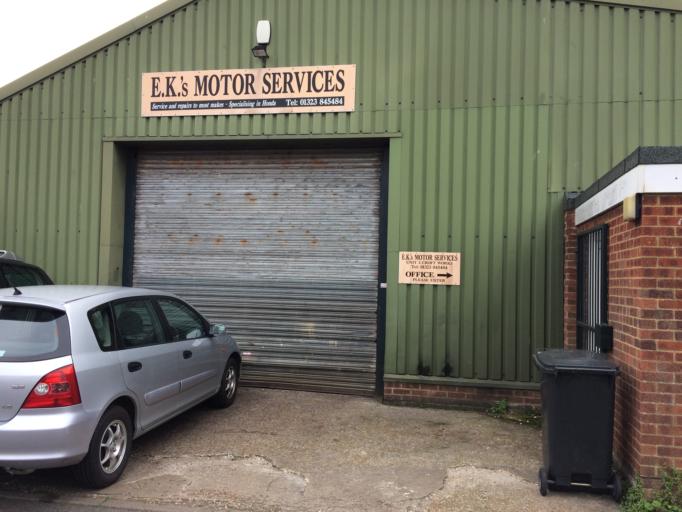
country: GB
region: England
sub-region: East Sussex
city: Hailsham
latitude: 50.8603
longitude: 0.2529
